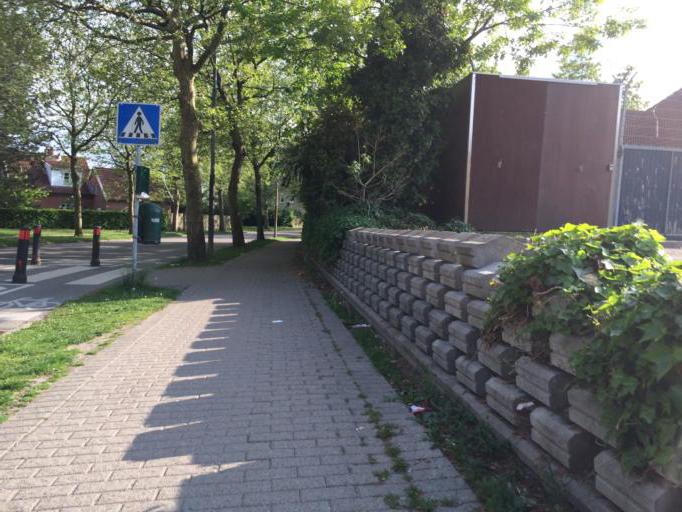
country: DK
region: Capital Region
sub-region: Hoje-Taastrup Kommune
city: Taastrup
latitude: 55.6506
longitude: 12.3039
